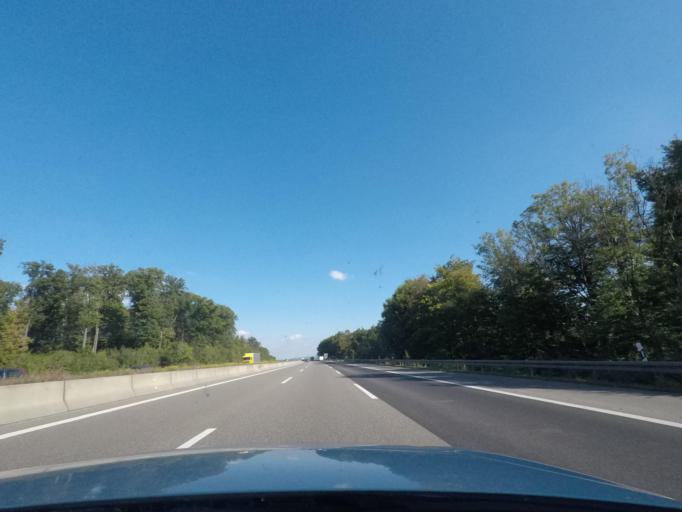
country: DE
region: Baden-Wuerttemberg
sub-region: Regierungsbezirk Stuttgart
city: Kirchardt
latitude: 49.2136
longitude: 9.0276
